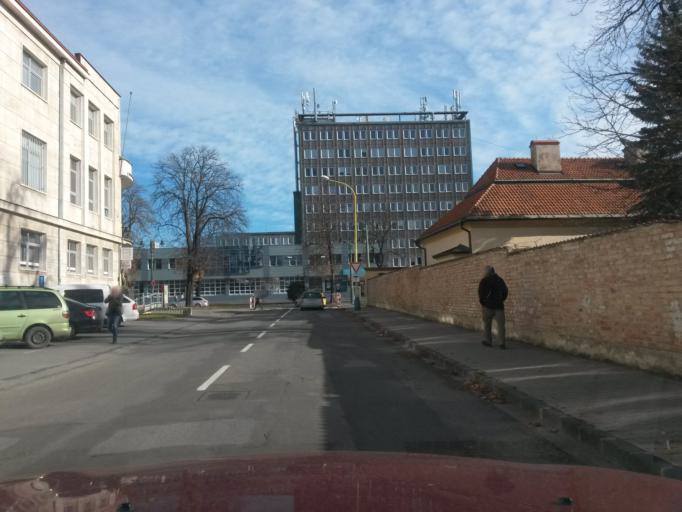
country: SK
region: Presovsky
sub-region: Okres Presov
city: Presov
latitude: 48.9905
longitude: 21.2452
